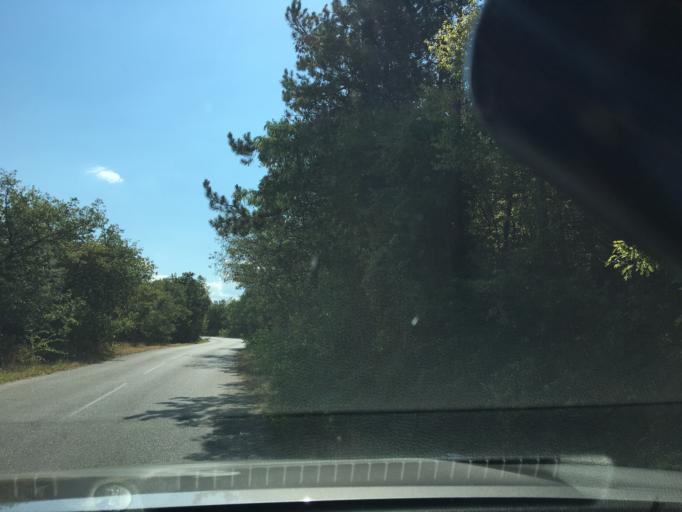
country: BG
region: Kyustendil
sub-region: Obshtina Boboshevo
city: Boboshevo
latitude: 42.1395
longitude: 23.0597
